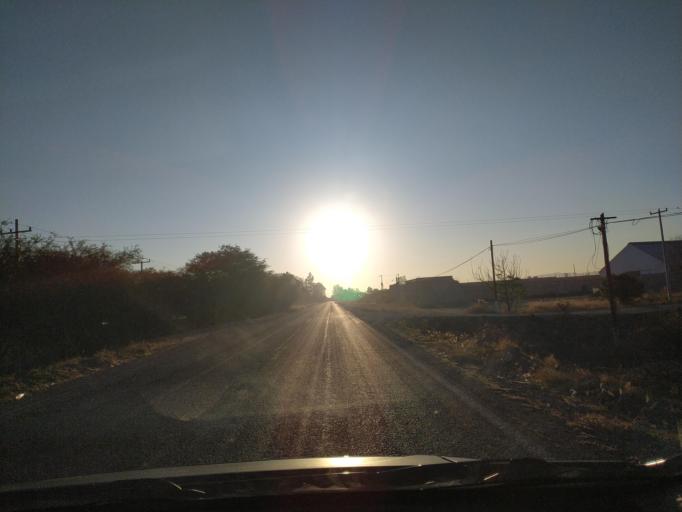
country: MX
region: Guanajuato
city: Ciudad Manuel Doblado
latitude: 20.7407
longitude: -101.9183
